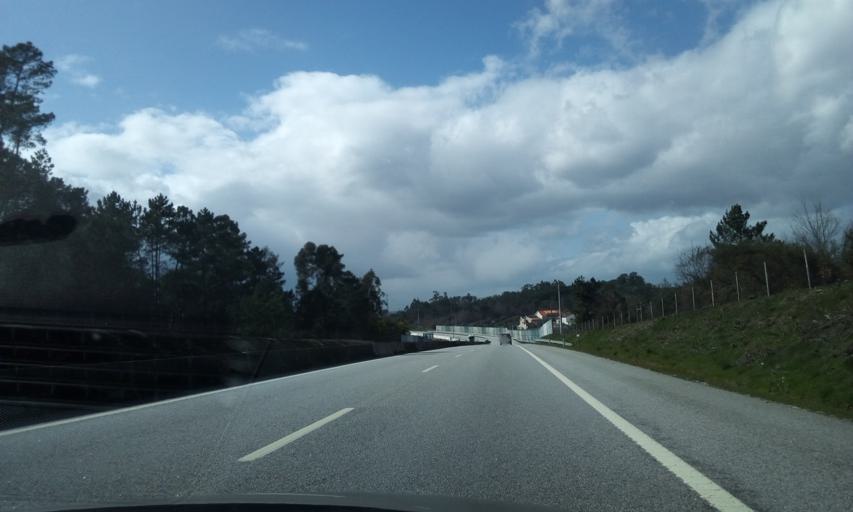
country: PT
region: Viseu
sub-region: Mangualde
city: Mangualde
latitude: 40.6213
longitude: -7.7686
